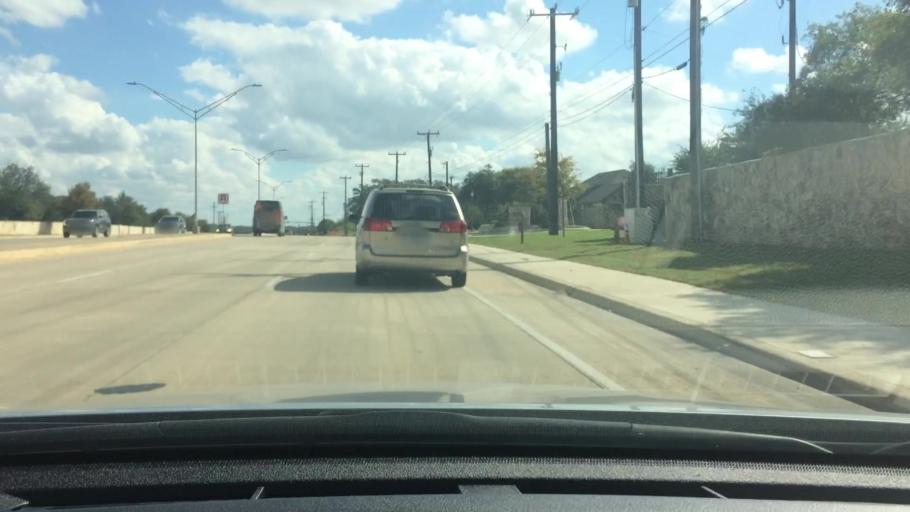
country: US
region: Texas
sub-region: Bexar County
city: Hollywood Park
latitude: 29.6111
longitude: -98.4208
